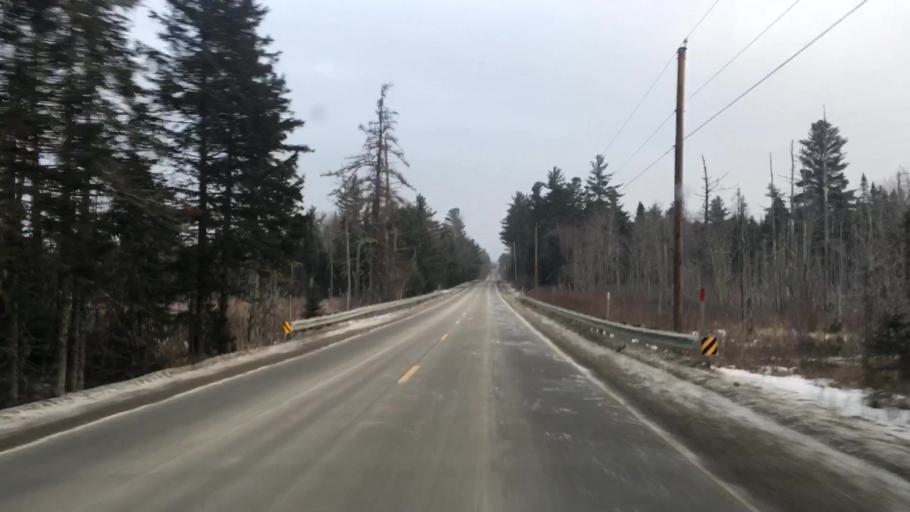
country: US
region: Maine
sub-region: Hancock County
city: Ellsworth
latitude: 44.6714
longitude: -68.3543
